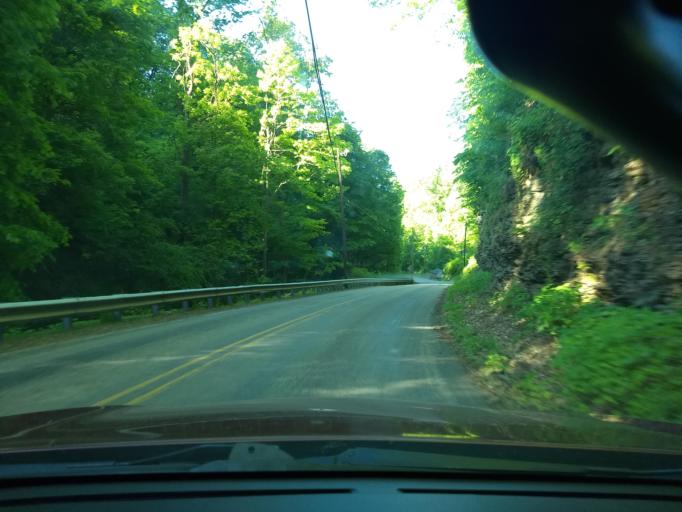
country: US
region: Pennsylvania
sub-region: Allegheny County
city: Versailles
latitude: 40.3042
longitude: -79.8402
